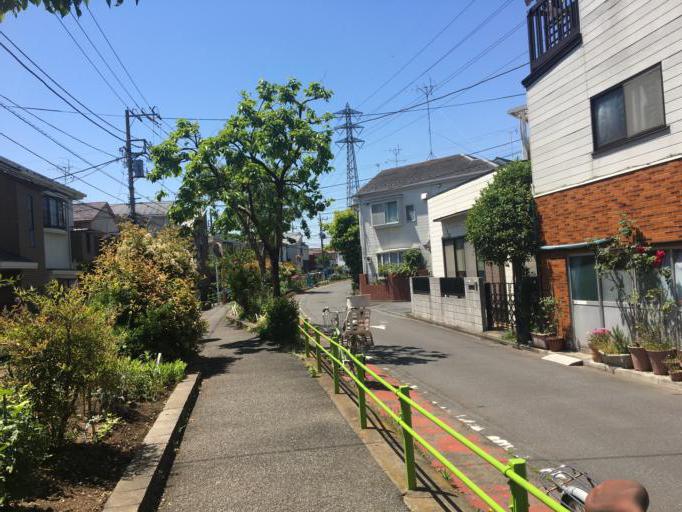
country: JP
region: Saitama
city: Wako
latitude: 35.7643
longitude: 139.6529
